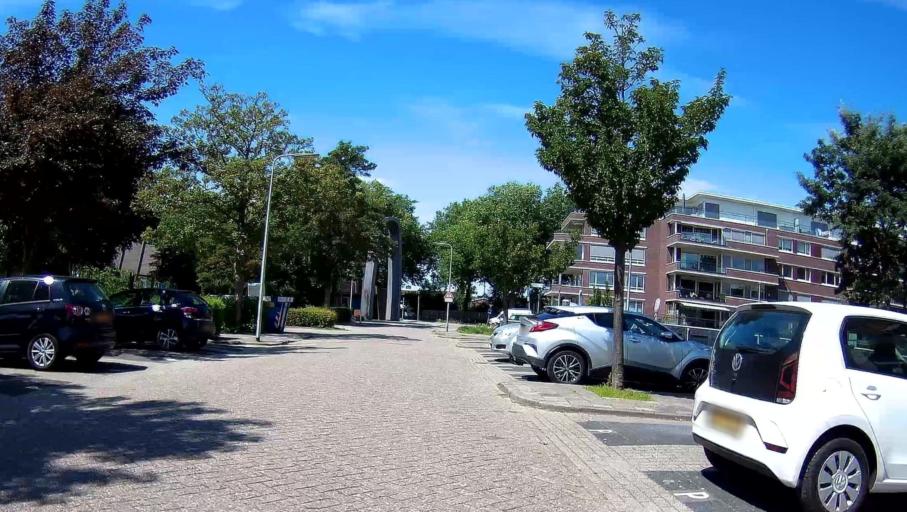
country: NL
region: South Holland
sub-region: Gemeente Krimpen aan den IJssel
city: Krimpen aan den IJssel
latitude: 51.9129
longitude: 4.5958
